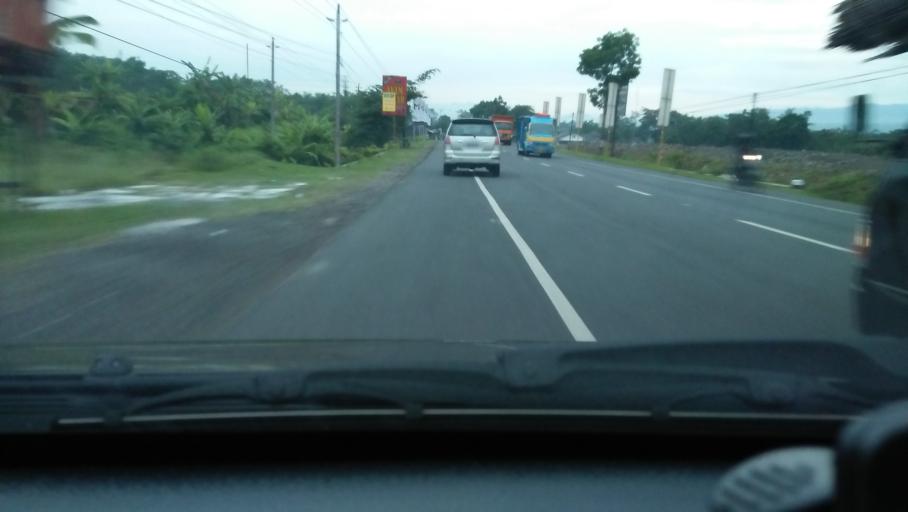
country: ID
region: Central Java
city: Magelang
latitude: -7.4114
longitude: 110.2367
